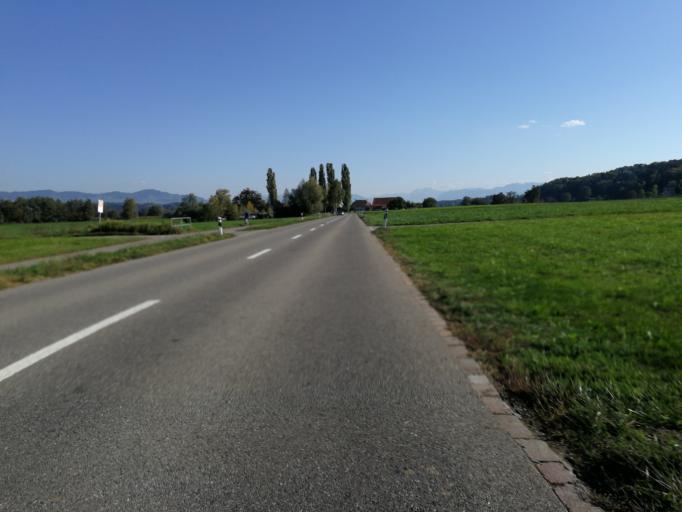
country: CH
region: Zurich
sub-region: Bezirk Uster
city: Hinteregg
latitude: 47.3202
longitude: 8.6926
